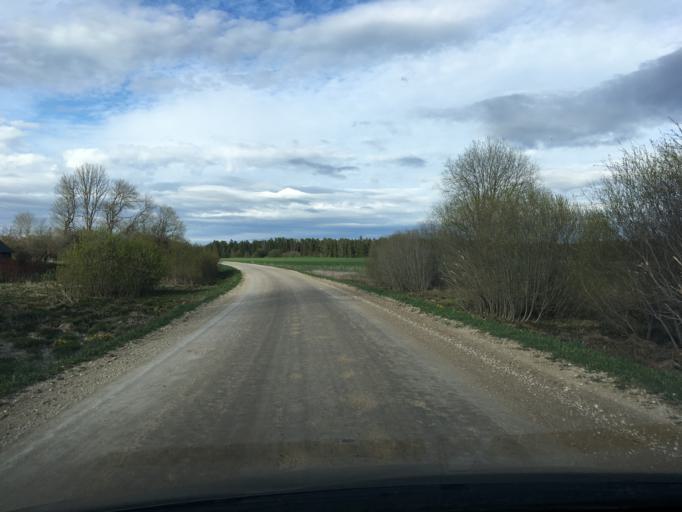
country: EE
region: Raplamaa
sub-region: Maerjamaa vald
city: Marjamaa
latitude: 59.0037
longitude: 24.3885
